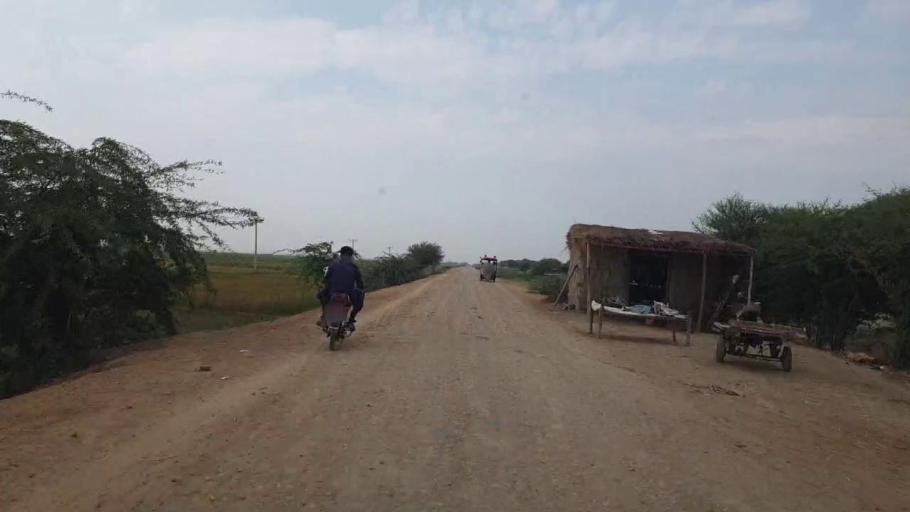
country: PK
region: Sindh
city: Kario
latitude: 24.6104
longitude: 68.5925
